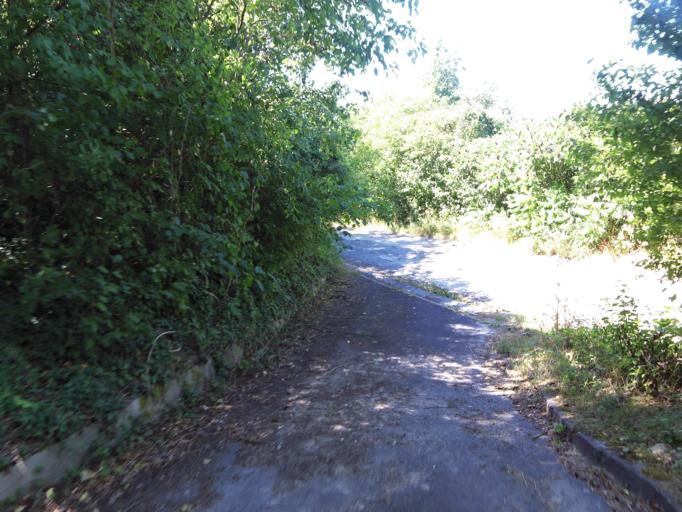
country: DE
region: Bavaria
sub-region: Regierungsbezirk Unterfranken
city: Randersacker
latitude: 49.7591
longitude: 9.9858
